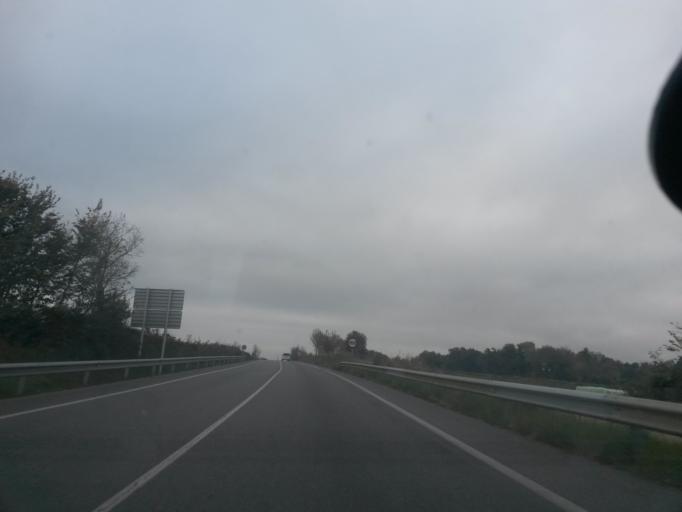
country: ES
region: Catalonia
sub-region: Provincia de Girona
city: Banyoles
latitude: 42.1250
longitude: 2.7823
